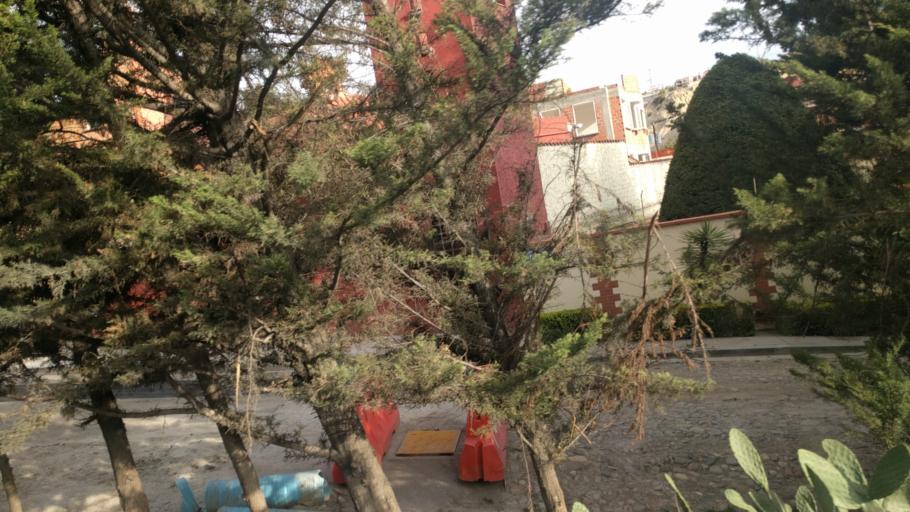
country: BO
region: La Paz
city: La Paz
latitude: -16.5595
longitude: -68.0942
